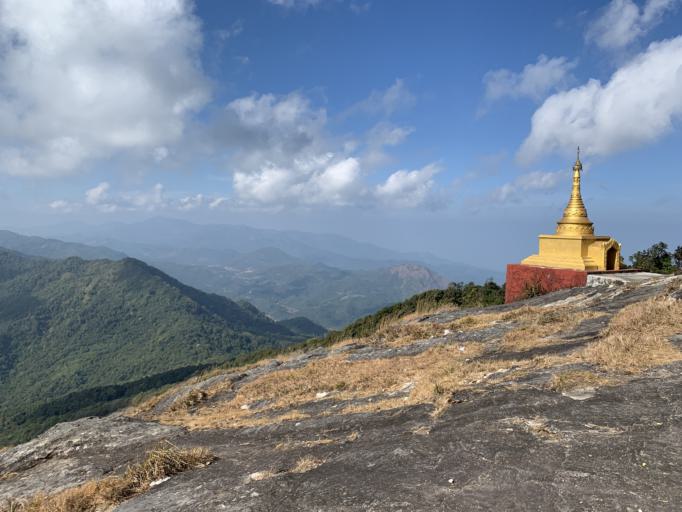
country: MM
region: Mandalay
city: Mogok
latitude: 22.9696
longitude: 96.6502
